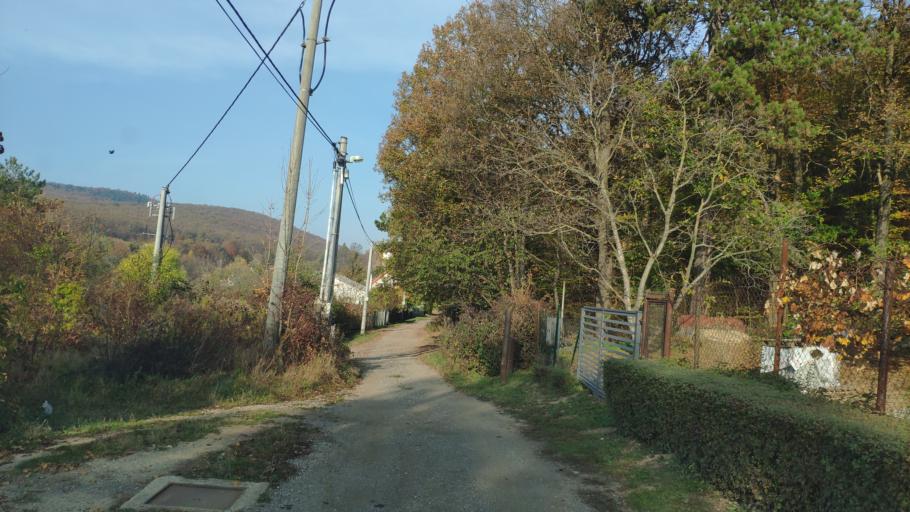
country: SK
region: Kosicky
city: Kosice
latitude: 48.7426
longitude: 21.2184
